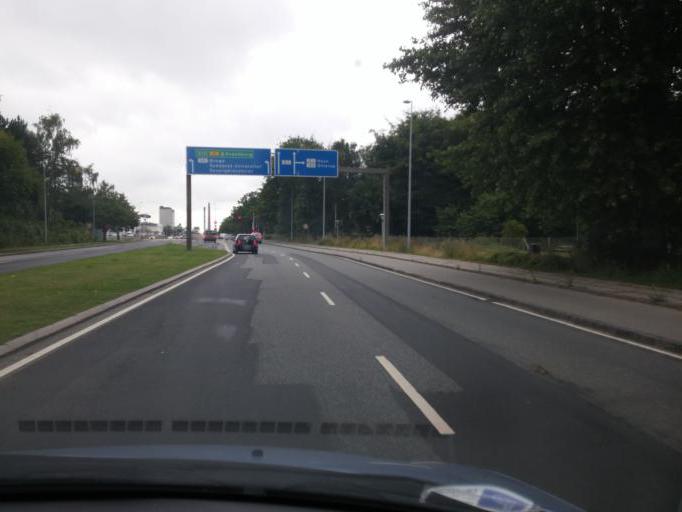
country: DK
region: South Denmark
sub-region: Odense Kommune
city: Neder Holluf
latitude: 55.3880
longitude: 10.4294
